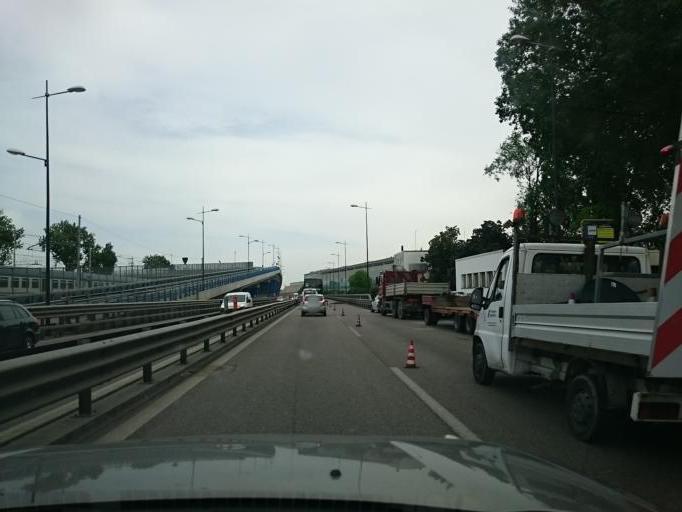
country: IT
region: Veneto
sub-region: Provincia di Venezia
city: Mestre
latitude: 45.4749
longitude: 12.2521
